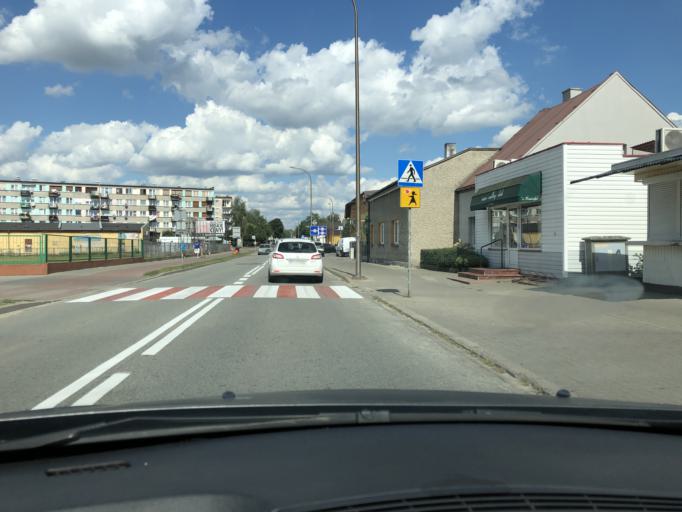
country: PL
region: Lodz Voivodeship
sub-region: Powiat wieruszowski
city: Wieruszow
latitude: 51.2956
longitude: 18.1608
